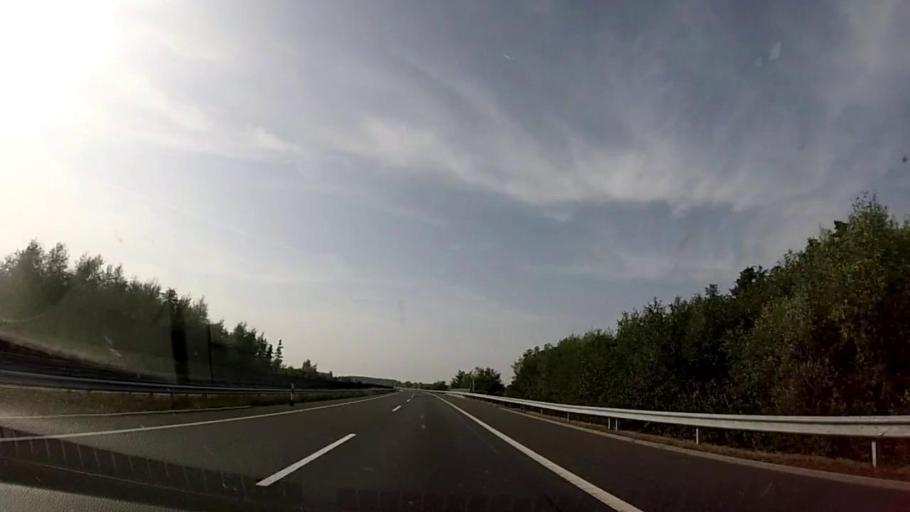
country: HU
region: Somogy
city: Balatonbereny
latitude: 46.6445
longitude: 17.2902
